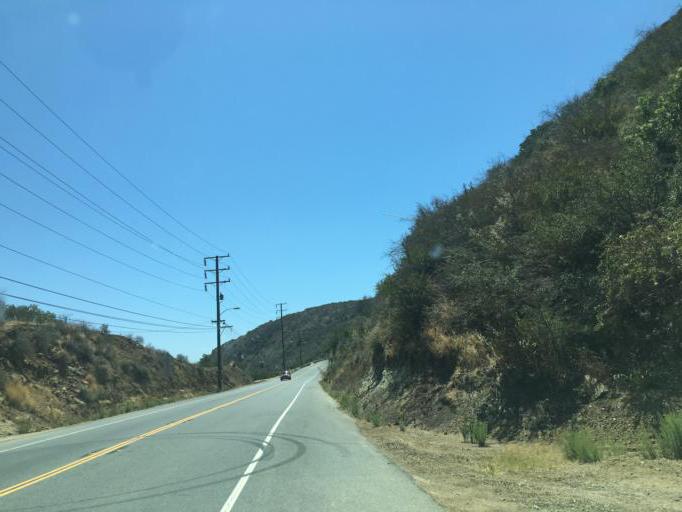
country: US
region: California
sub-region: Los Angeles County
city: Malibu Beach
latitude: 34.0495
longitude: -118.6932
